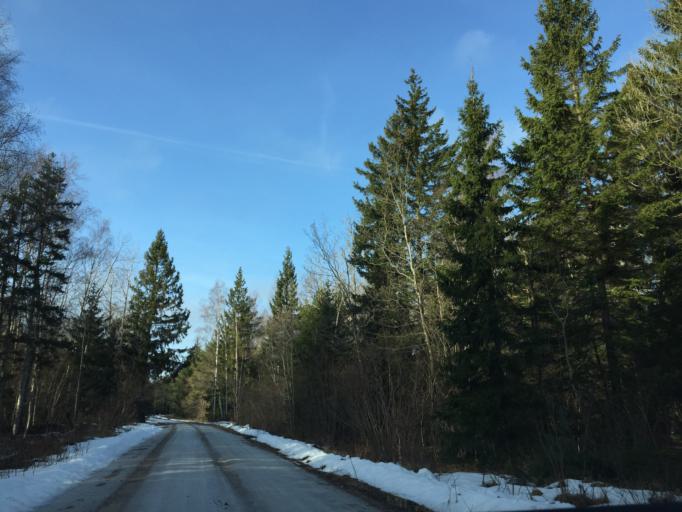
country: EE
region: Saare
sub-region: Kuressaare linn
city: Kuressaare
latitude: 58.4686
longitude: 21.9804
